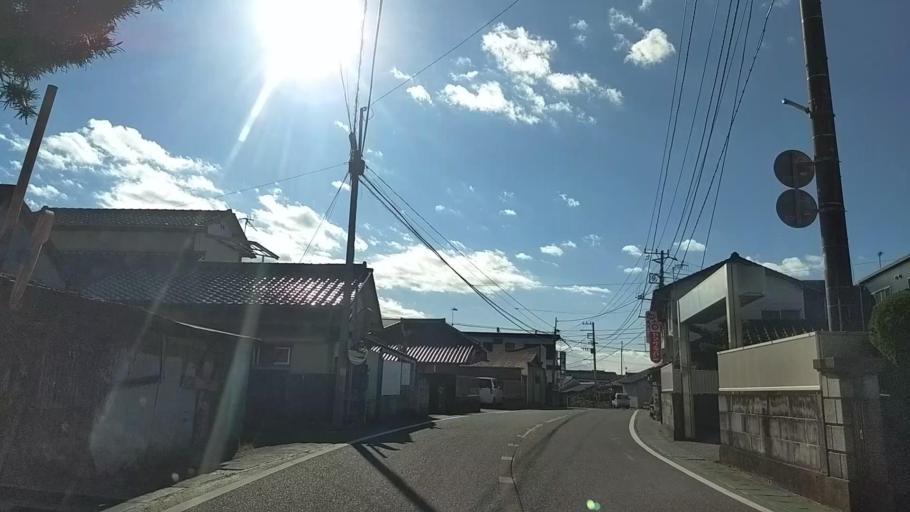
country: JP
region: Chiba
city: Tateyama
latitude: 35.0629
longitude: 139.8271
